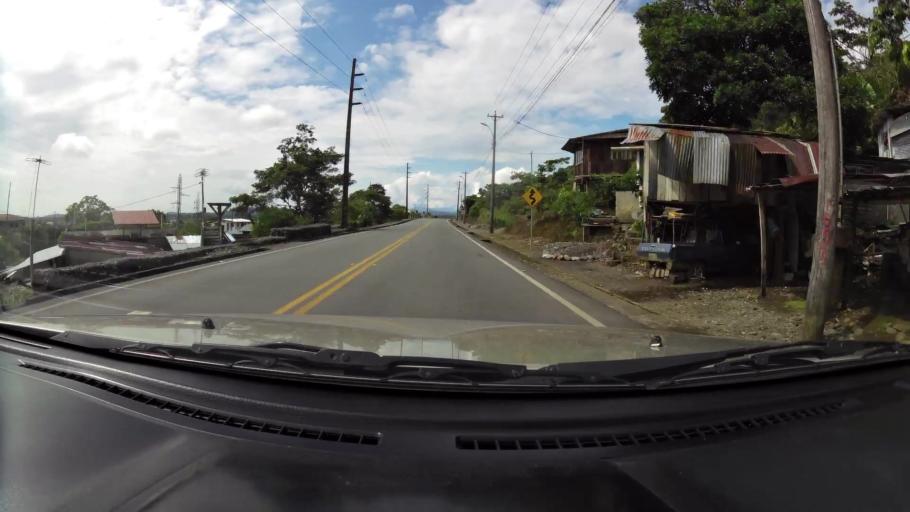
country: EC
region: Pastaza
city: Puyo
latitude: -1.4905
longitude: -78.0168
